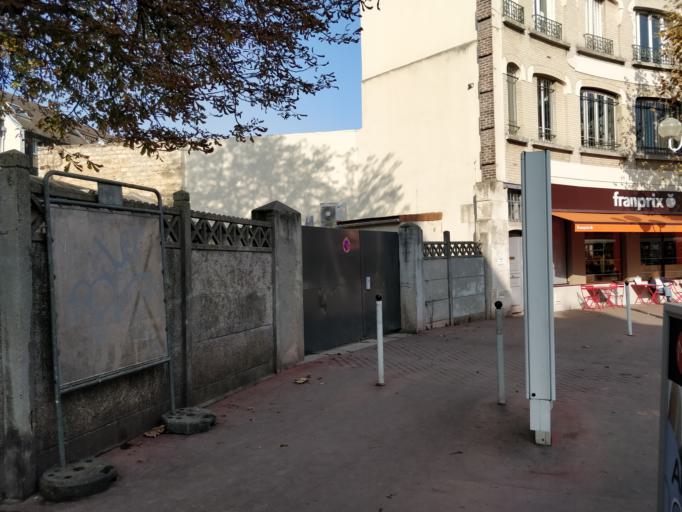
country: FR
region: Ile-de-France
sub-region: Departement des Hauts-de-Seine
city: Montrouge
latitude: 48.8173
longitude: 2.3185
